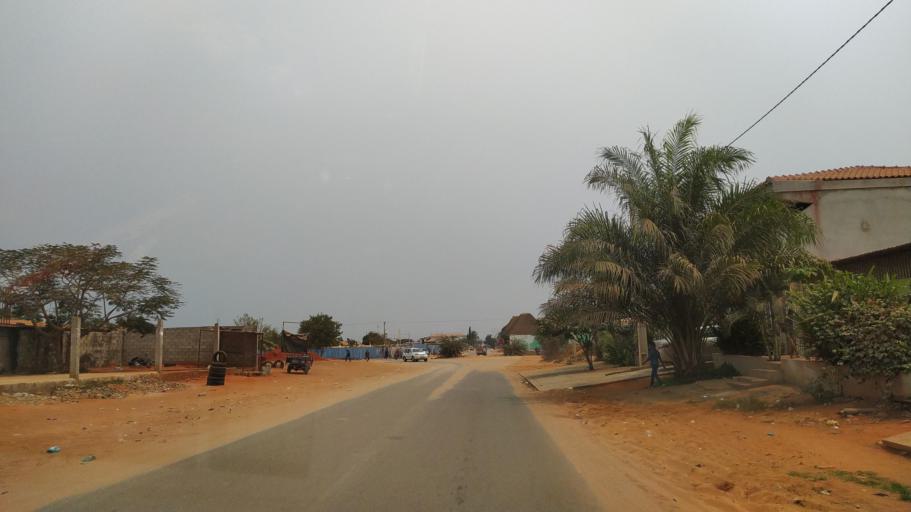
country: AO
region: Luanda
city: Luanda
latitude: -9.0707
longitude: 13.4131
